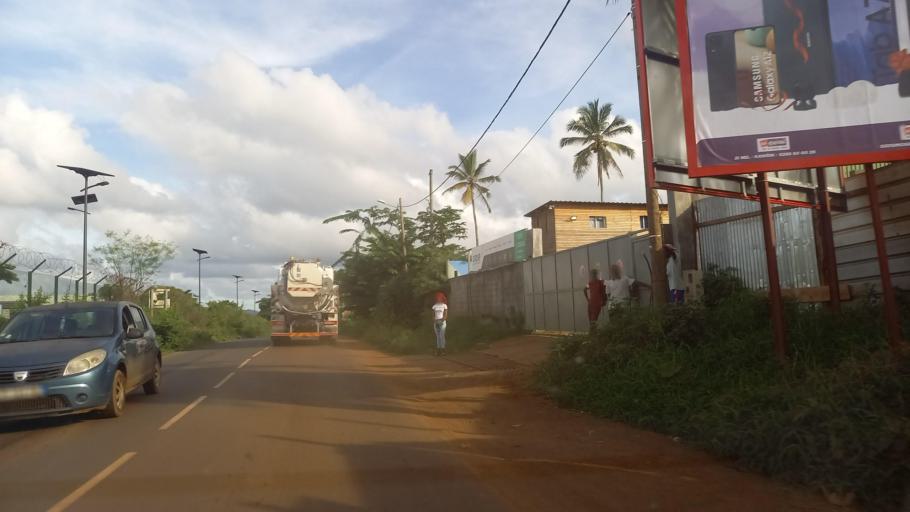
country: YT
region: Ouangani
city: Ouangani
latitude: -12.8230
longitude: 45.1324
